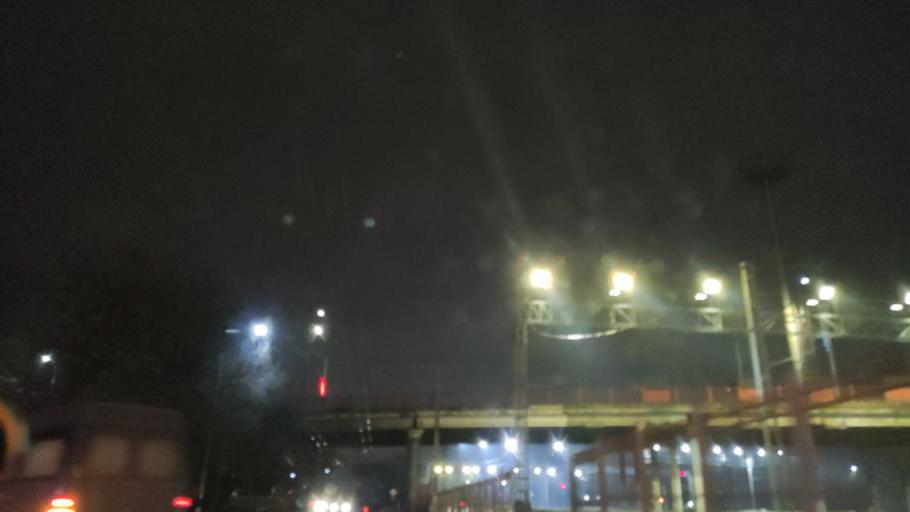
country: RU
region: Moskovskaya
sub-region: Podol'skiy Rayon
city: Podol'sk
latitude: 55.4256
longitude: 37.5629
